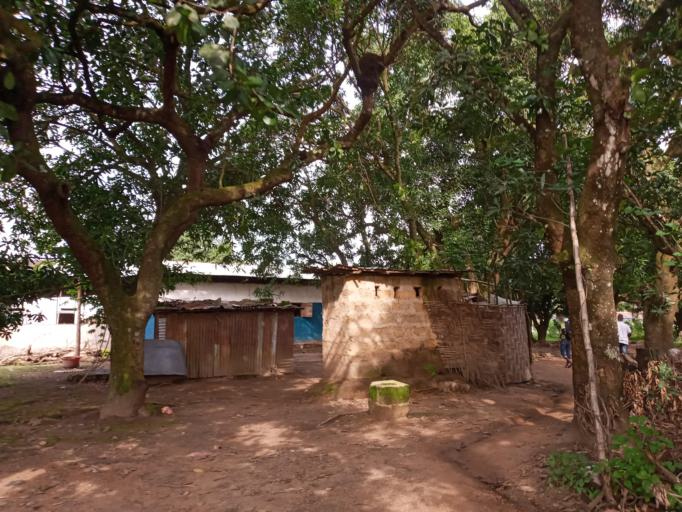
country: SL
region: Northern Province
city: Bumbuna
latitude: 9.0464
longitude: -11.7532
